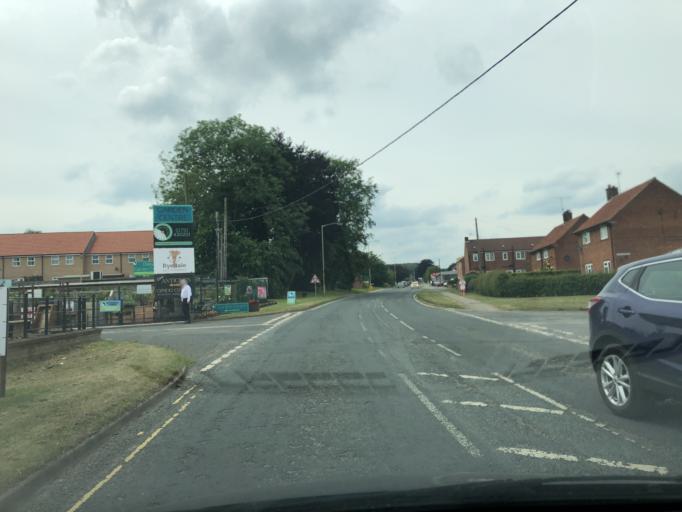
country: GB
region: England
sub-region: North Yorkshire
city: Great Habton
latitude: 54.2658
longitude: -0.9269
